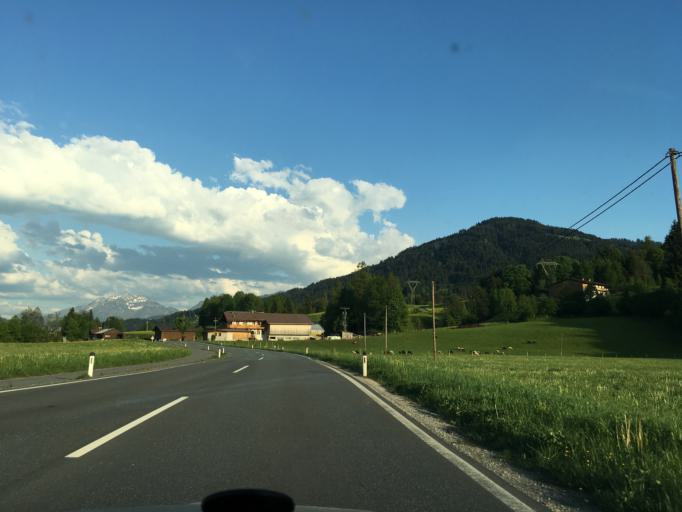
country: AT
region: Tyrol
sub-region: Politischer Bezirk Kitzbuhel
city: Sankt Johann in Tirol
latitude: 47.5108
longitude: 12.4594
